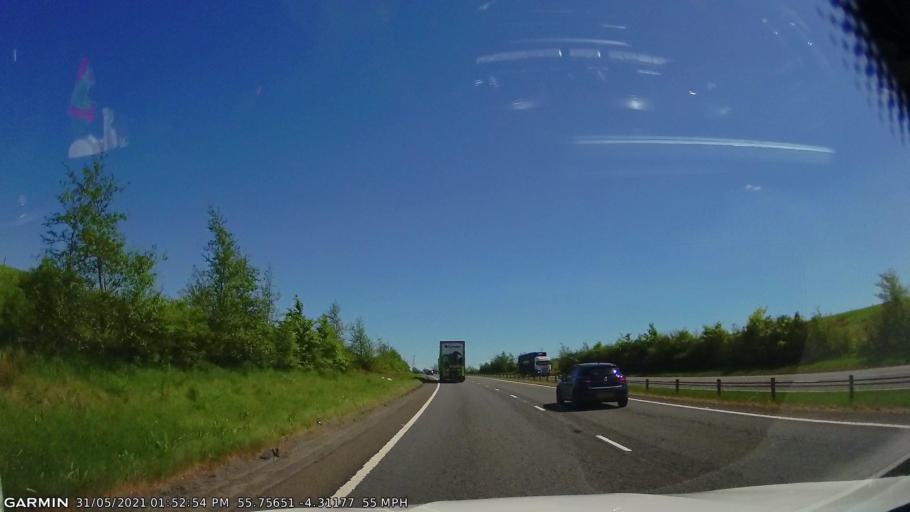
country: GB
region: Scotland
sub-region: East Renfrewshire
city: Newton Mearns
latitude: 55.7566
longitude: -4.3121
